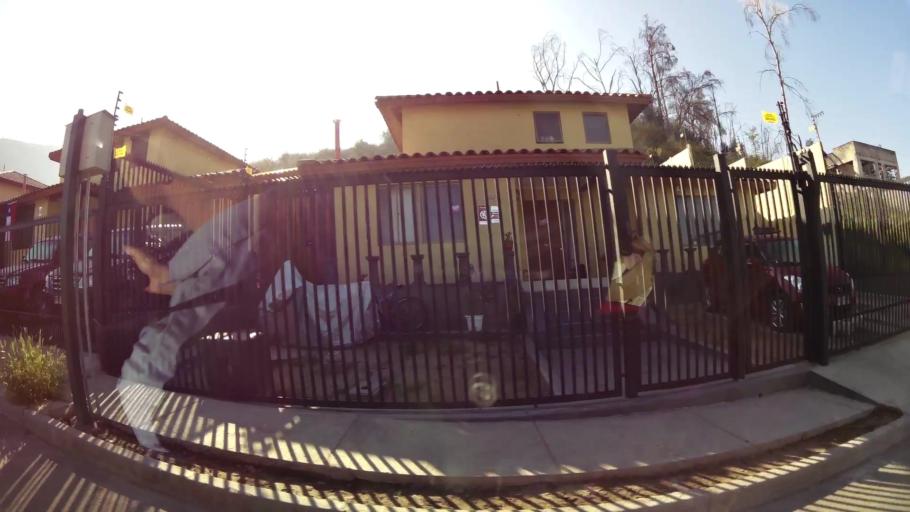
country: CL
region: Santiago Metropolitan
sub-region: Provincia de Chacabuco
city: Chicureo Abajo
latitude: -33.3558
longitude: -70.6594
